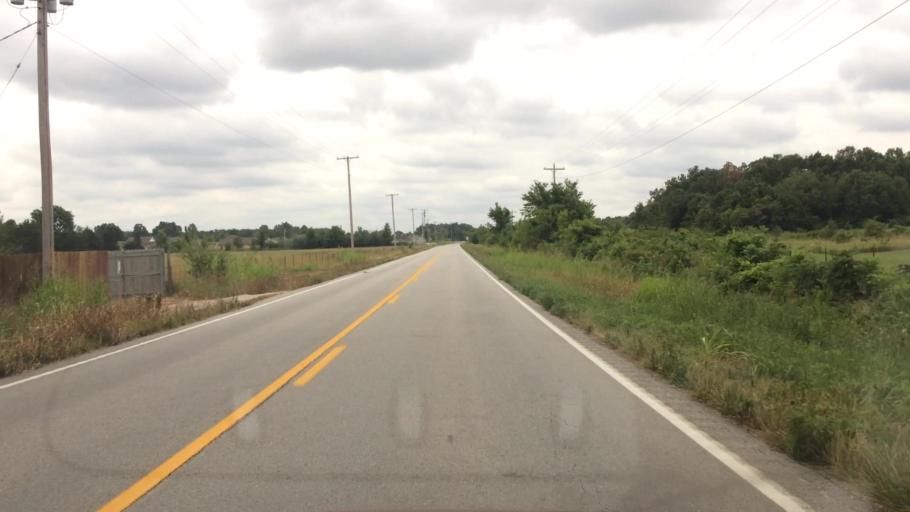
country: US
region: Missouri
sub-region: Greene County
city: Strafford
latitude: 37.2879
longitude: -93.1131
